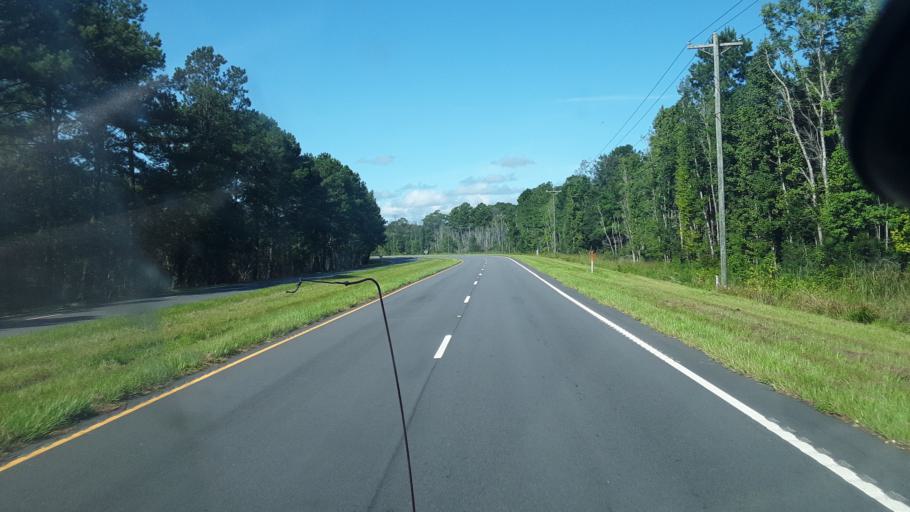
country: US
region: South Carolina
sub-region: Hampton County
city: Yemassee
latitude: 32.5922
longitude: -80.9212
